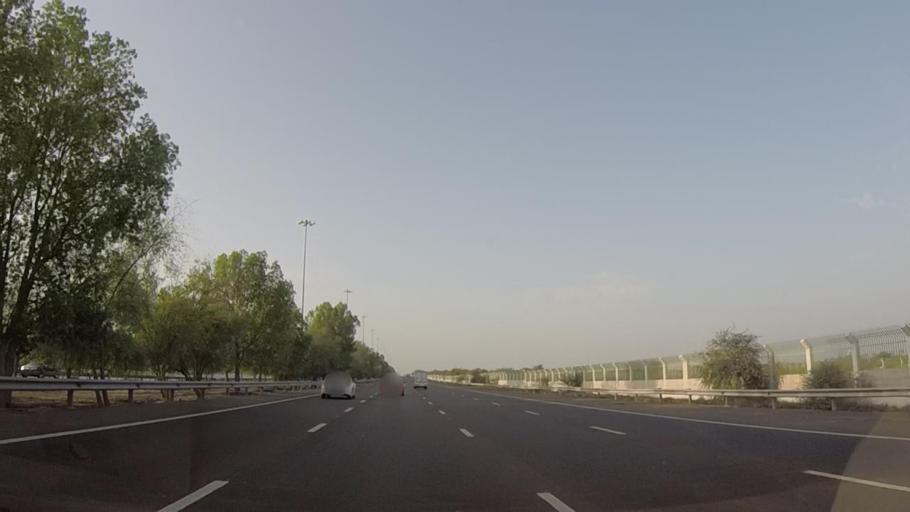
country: AE
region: Dubai
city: Dubai
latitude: 24.8337
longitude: 54.8849
